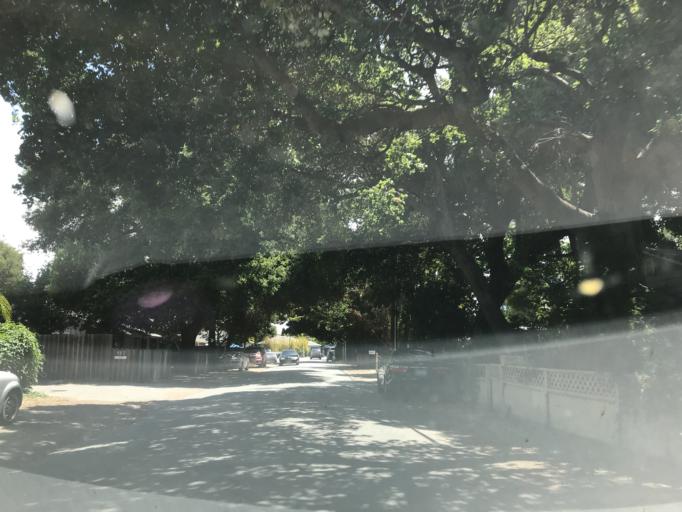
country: US
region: California
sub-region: San Mateo County
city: East Palo Alto
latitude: 37.4643
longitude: -122.1361
